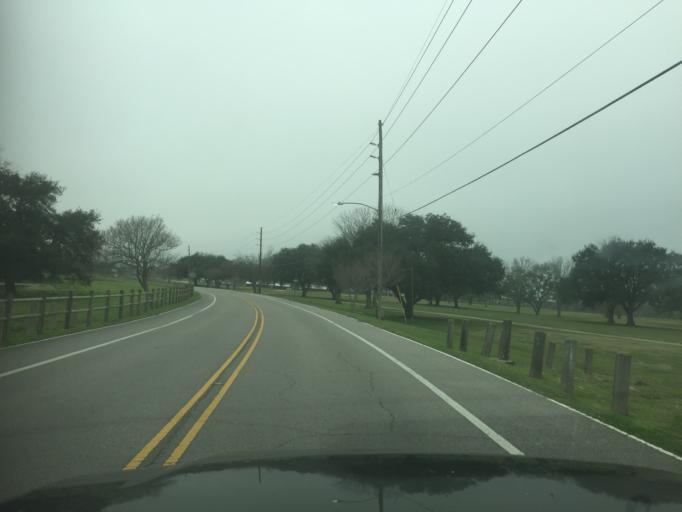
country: US
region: Louisiana
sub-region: Orleans Parish
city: New Orleans
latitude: 30.0123
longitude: -90.0912
